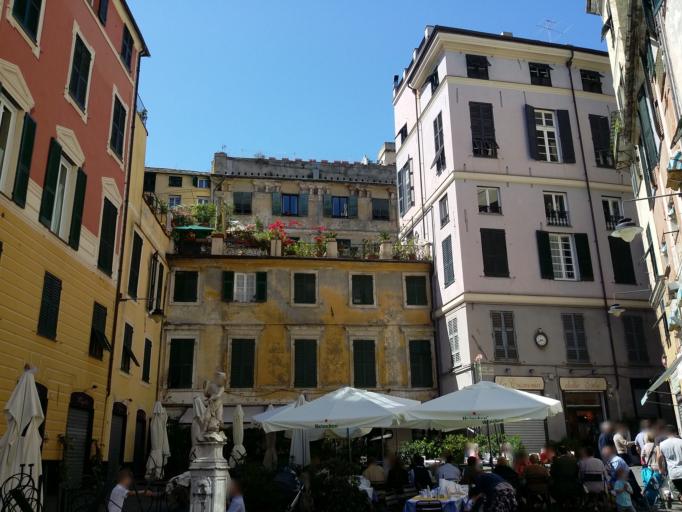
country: IT
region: Liguria
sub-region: Provincia di Genova
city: San Teodoro
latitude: 44.4061
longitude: 8.9326
